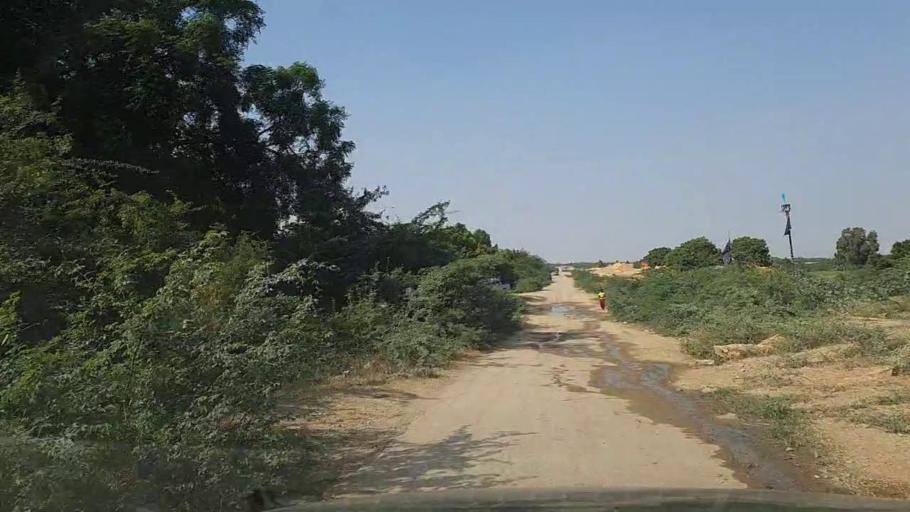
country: PK
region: Sindh
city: Gharo
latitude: 24.7543
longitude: 67.5805
